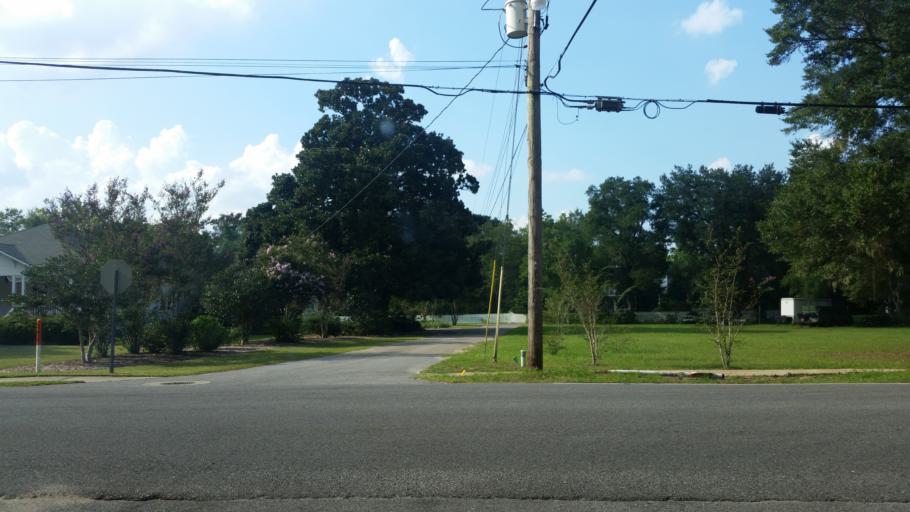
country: US
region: Florida
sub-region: Santa Rosa County
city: Bagdad
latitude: 30.6038
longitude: -87.0354
